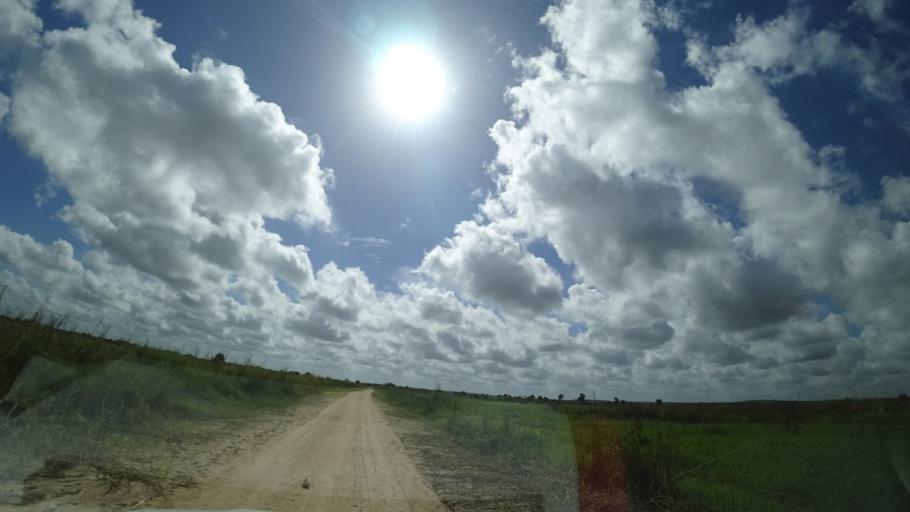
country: MZ
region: Sofala
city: Dondo
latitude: -19.3937
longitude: 34.5743
